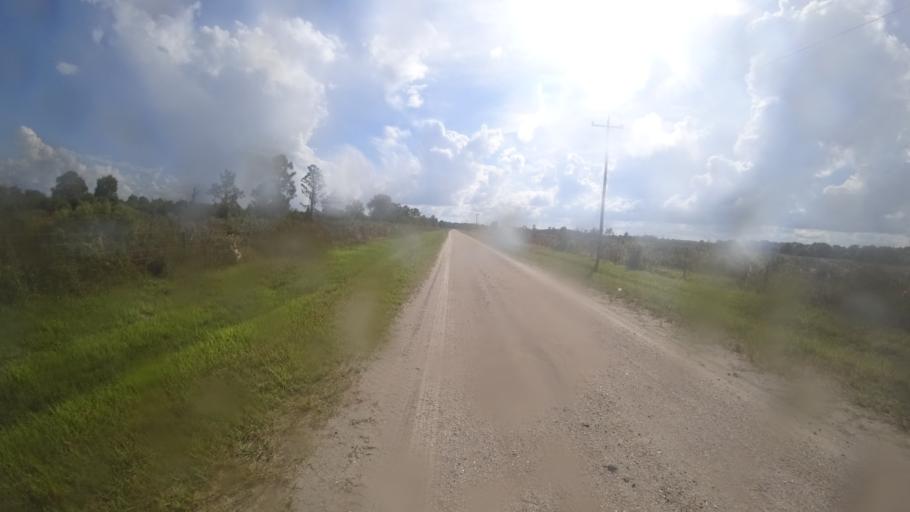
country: US
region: Florida
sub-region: Hillsborough County
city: Wimauma
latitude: 27.6012
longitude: -82.1197
